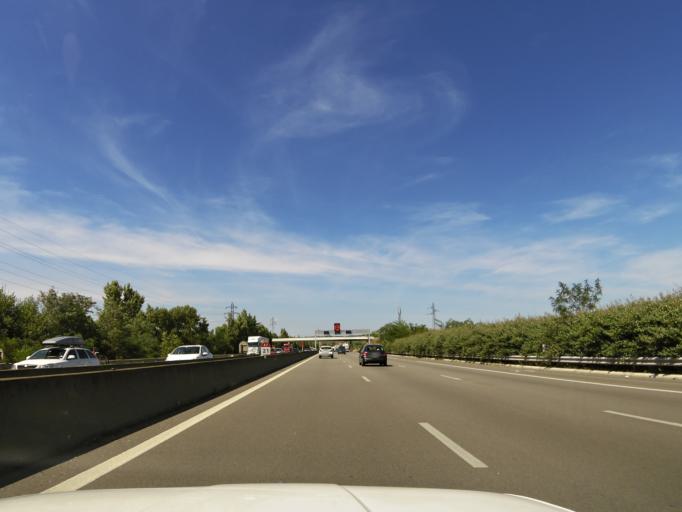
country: FR
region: Rhone-Alpes
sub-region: Departement de l'Isere
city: Salaise-sur-Sanne
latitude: 45.3469
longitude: 4.8070
